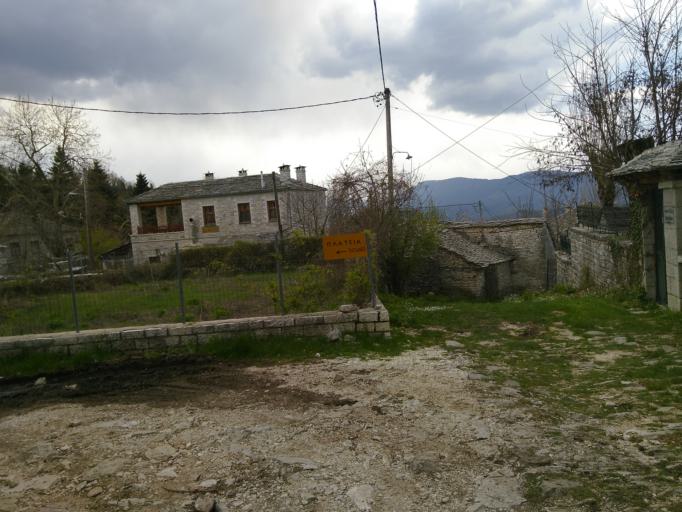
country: GR
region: Epirus
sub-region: Nomos Ioanninon
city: Asprangeloi
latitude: 39.8826
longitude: 20.7483
